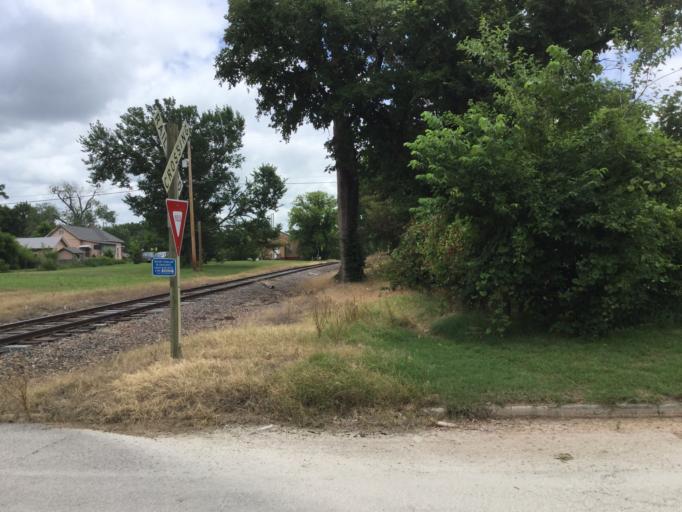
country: US
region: Kansas
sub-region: Montgomery County
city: Independence
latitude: 37.2175
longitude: -95.7212
